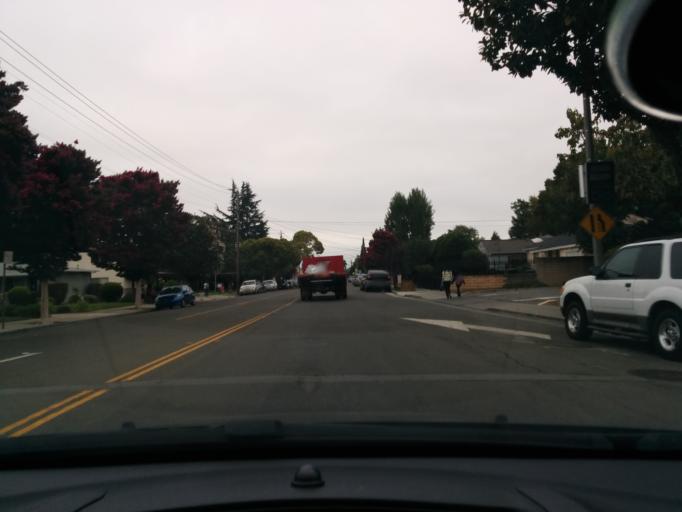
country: US
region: California
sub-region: Santa Clara County
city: Sunnyvale
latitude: 37.3890
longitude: -122.0284
